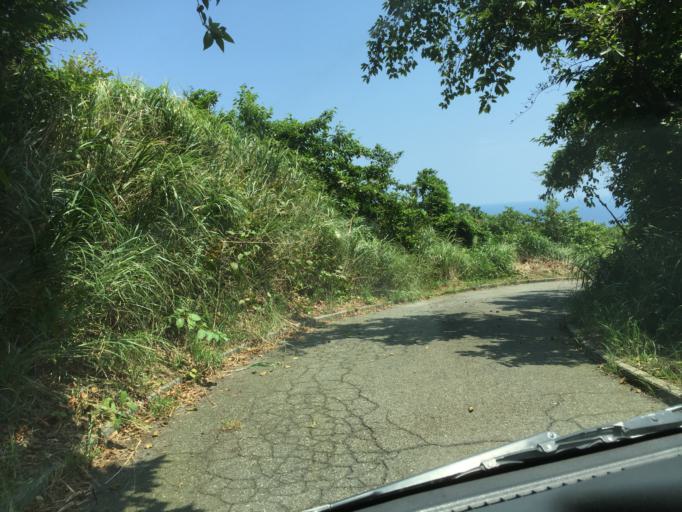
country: JP
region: Shizuoka
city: Shimoda
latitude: 34.1002
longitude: 139.5487
